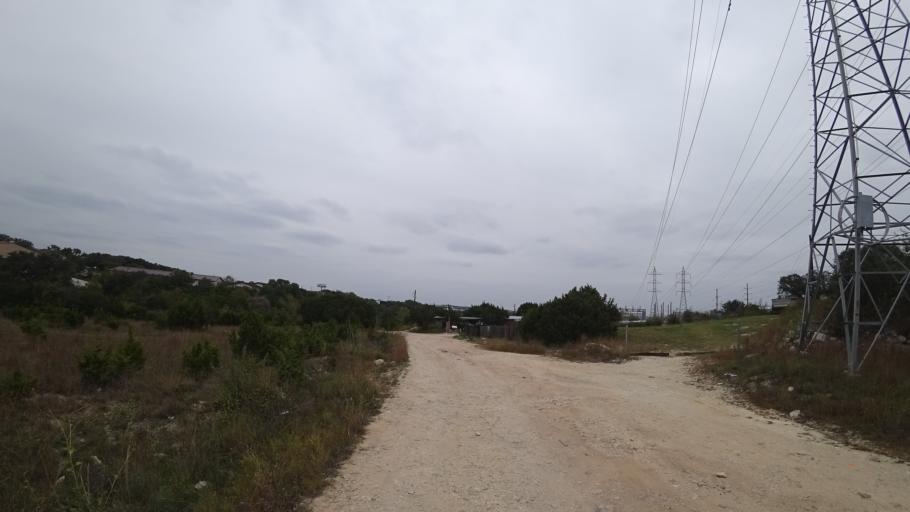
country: US
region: Texas
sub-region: Travis County
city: Lakeway
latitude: 30.3767
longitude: -97.9442
